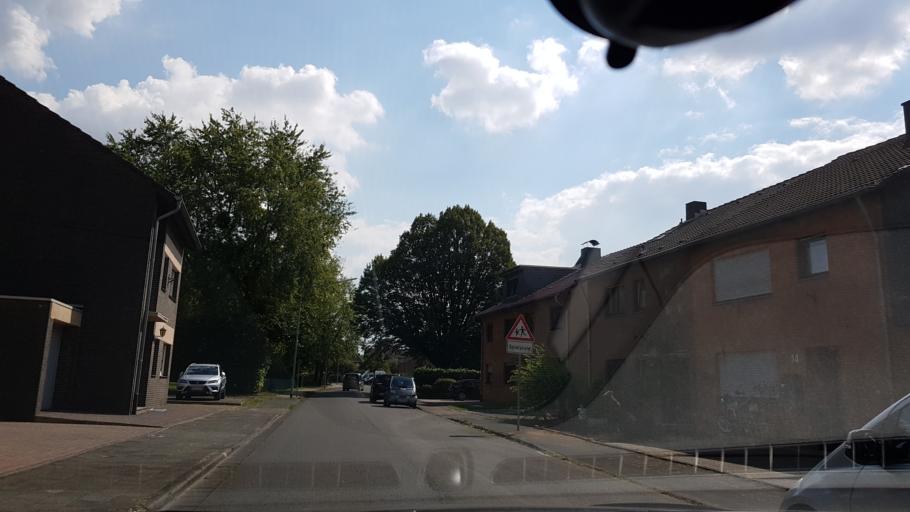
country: DE
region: North Rhine-Westphalia
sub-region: Regierungsbezirk Dusseldorf
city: Grevenbroich
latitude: 51.0471
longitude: 6.5801
